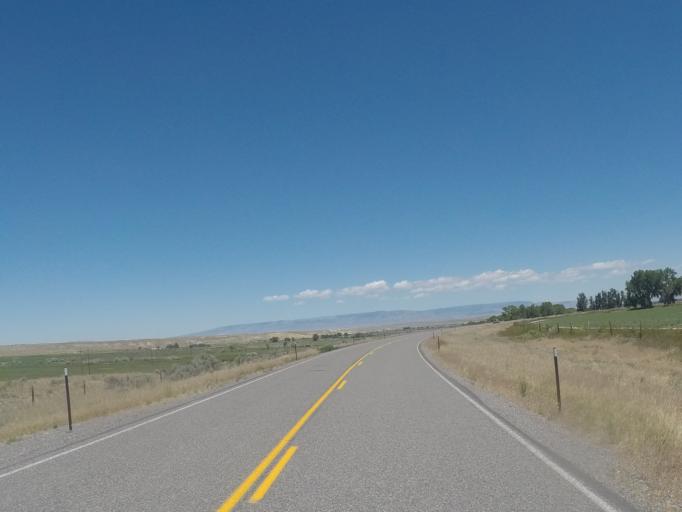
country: US
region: Wyoming
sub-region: Park County
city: Powell
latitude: 44.7452
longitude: -108.5796
